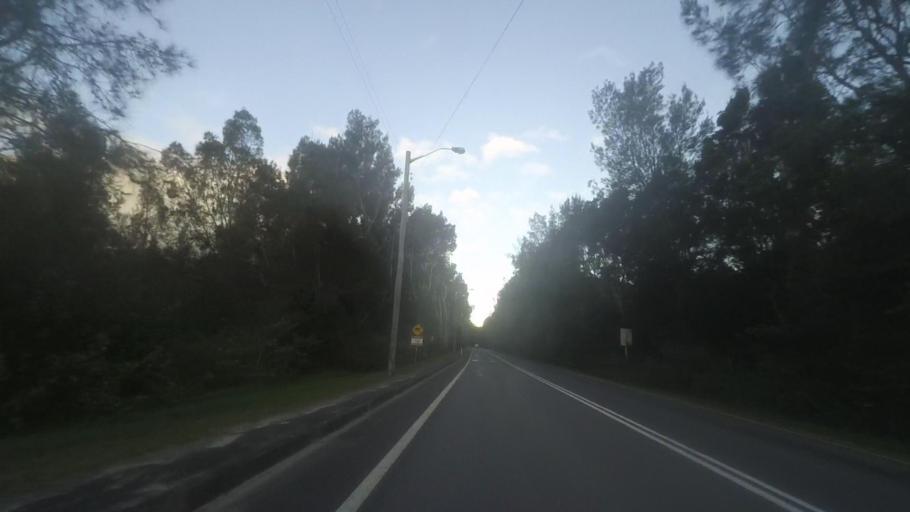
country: AU
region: New South Wales
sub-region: Great Lakes
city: Hawks Nest
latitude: -32.6683
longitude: 152.1703
